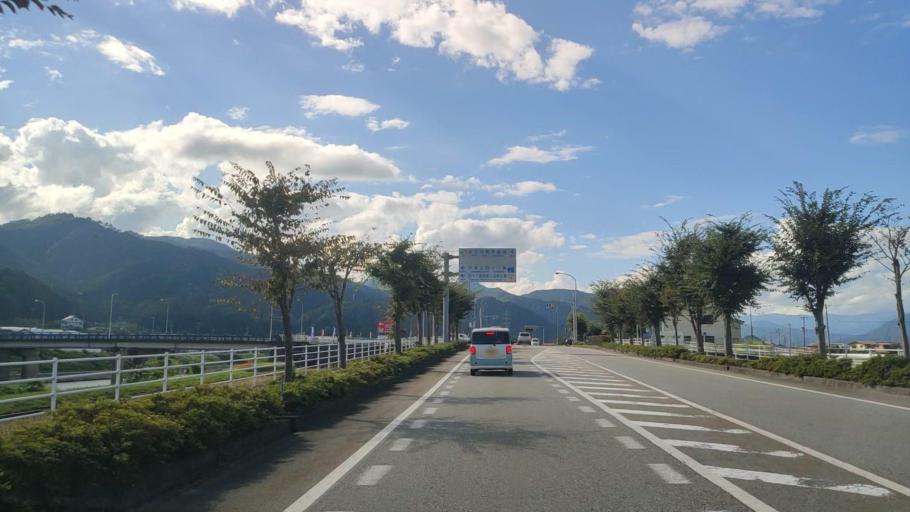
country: JP
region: Gifu
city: Takayama
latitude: 36.2166
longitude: 137.2024
